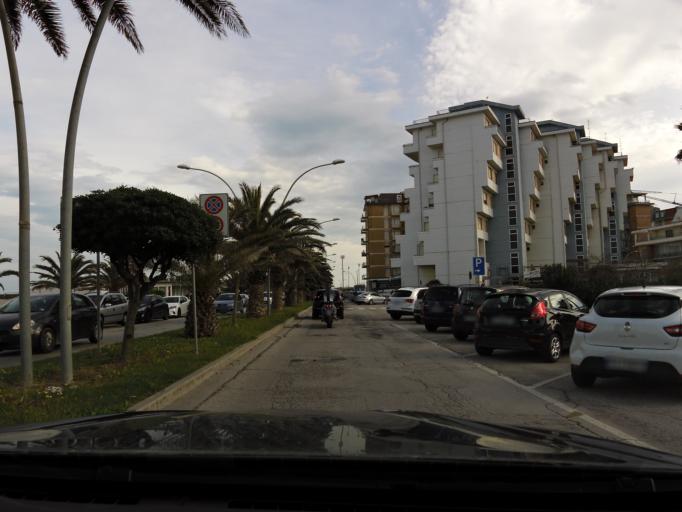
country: IT
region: The Marches
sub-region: Provincia di Macerata
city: Portocivitanova
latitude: 43.3017
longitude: 13.7375
